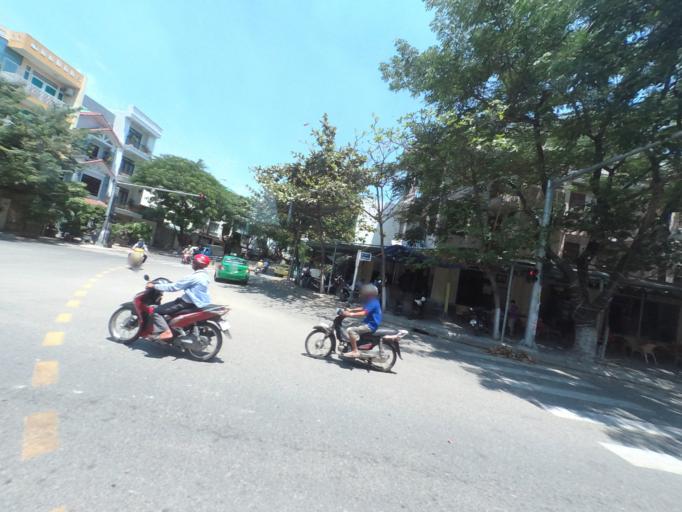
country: VN
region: Da Nang
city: Lien Chieu
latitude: 16.0721
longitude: 108.1736
